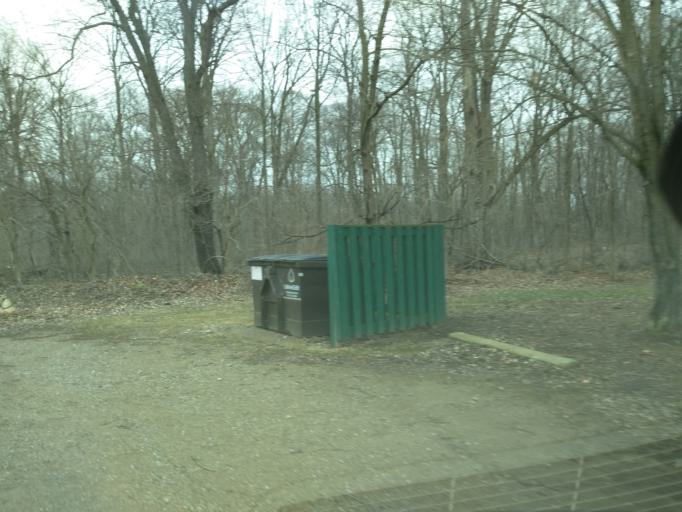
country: US
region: Michigan
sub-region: Ingham County
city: Edgemont Park
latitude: 42.7570
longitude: -84.6088
